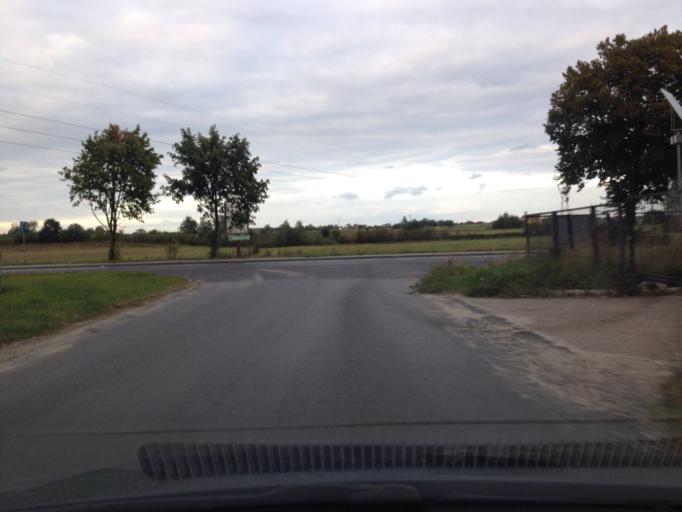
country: PL
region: Kujawsko-Pomorskie
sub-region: Powiat rypinski
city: Rypin
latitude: 53.0444
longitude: 19.4425
